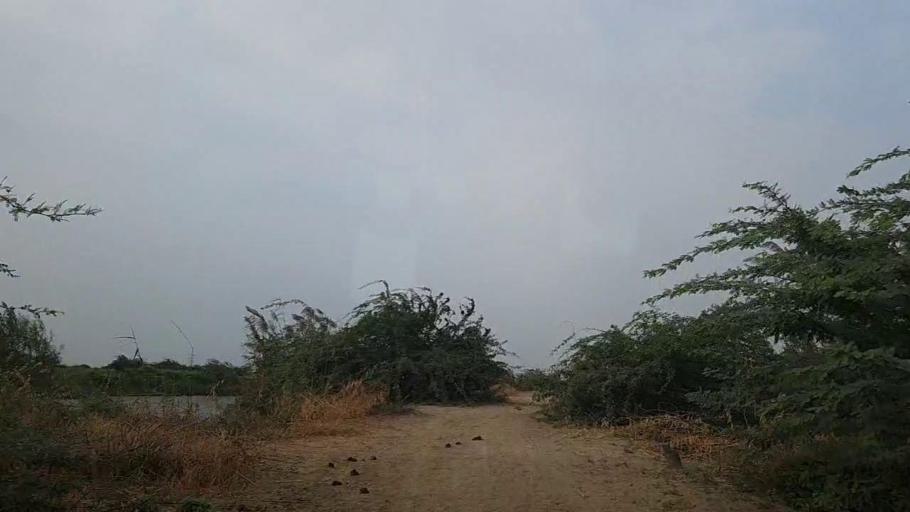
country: PK
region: Sindh
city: Mirpur Sakro
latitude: 24.6214
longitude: 67.5022
